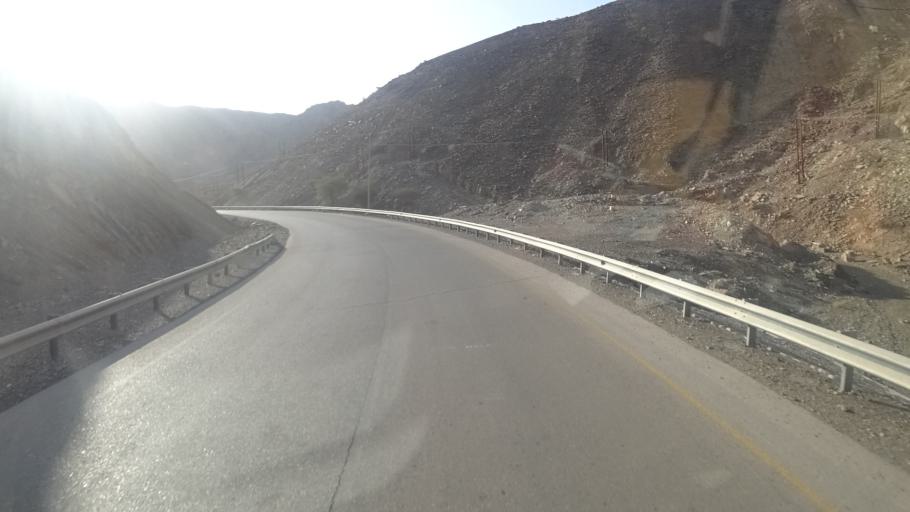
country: OM
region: Ash Sharqiyah
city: Badiyah
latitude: 22.5327
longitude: 58.9595
